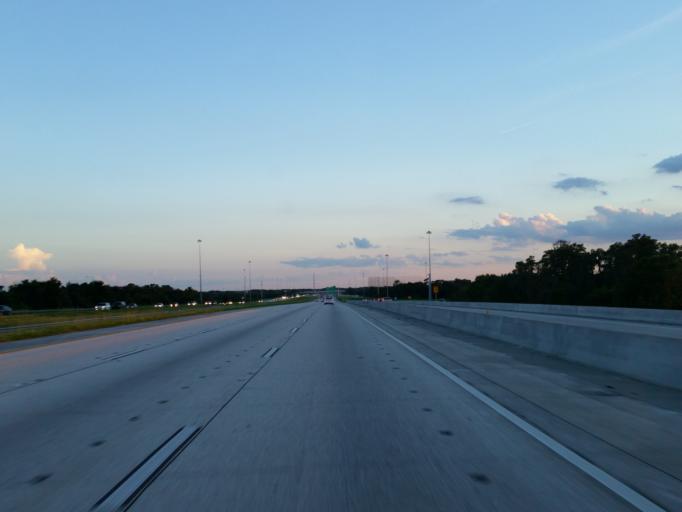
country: US
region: Florida
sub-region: Hillsborough County
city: Mango
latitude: 27.9492
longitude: -82.3286
